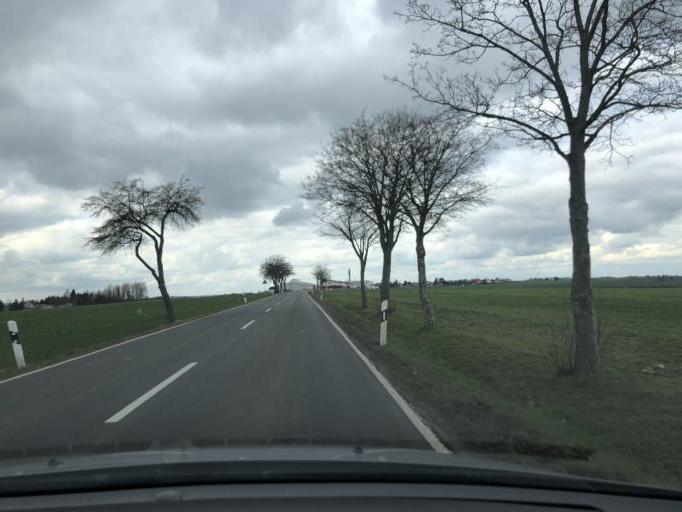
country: DE
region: Saxony
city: Grossweitzschen
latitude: 51.1539
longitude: 13.0677
